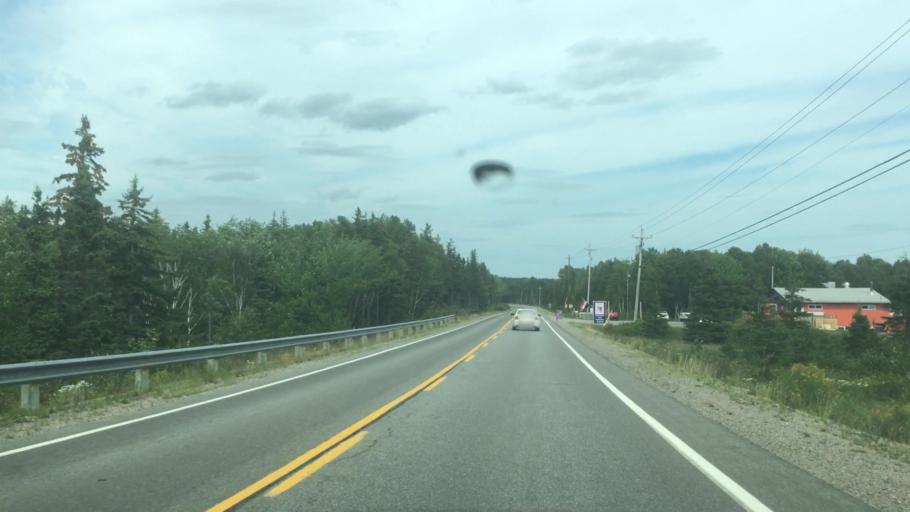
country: CA
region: Nova Scotia
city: Sydney Mines
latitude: 46.5057
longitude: -60.4340
